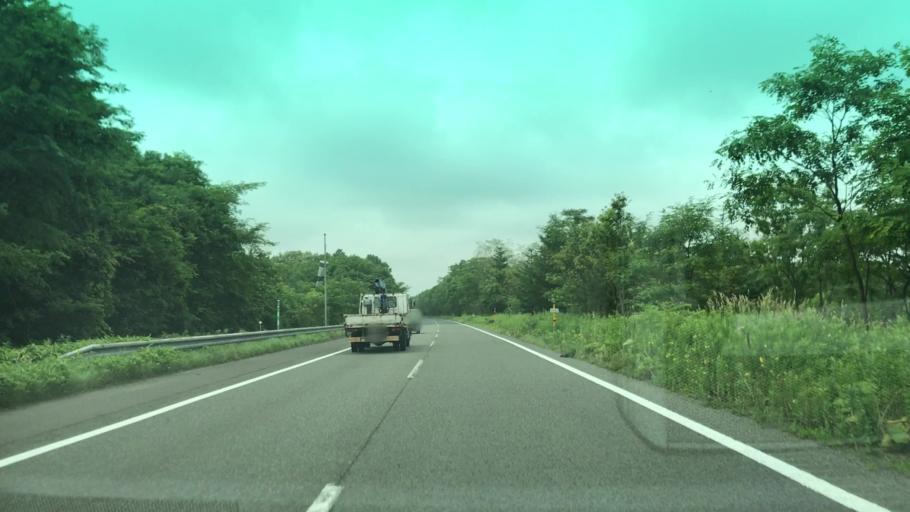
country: JP
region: Hokkaido
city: Chitose
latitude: 42.7451
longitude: 141.6491
